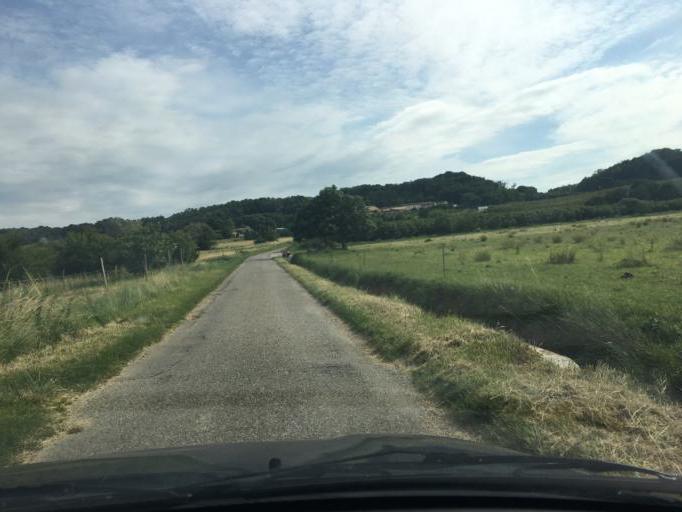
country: FR
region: Rhone-Alpes
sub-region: Departement de la Drome
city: Mercurol
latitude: 45.1021
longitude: 4.9124
